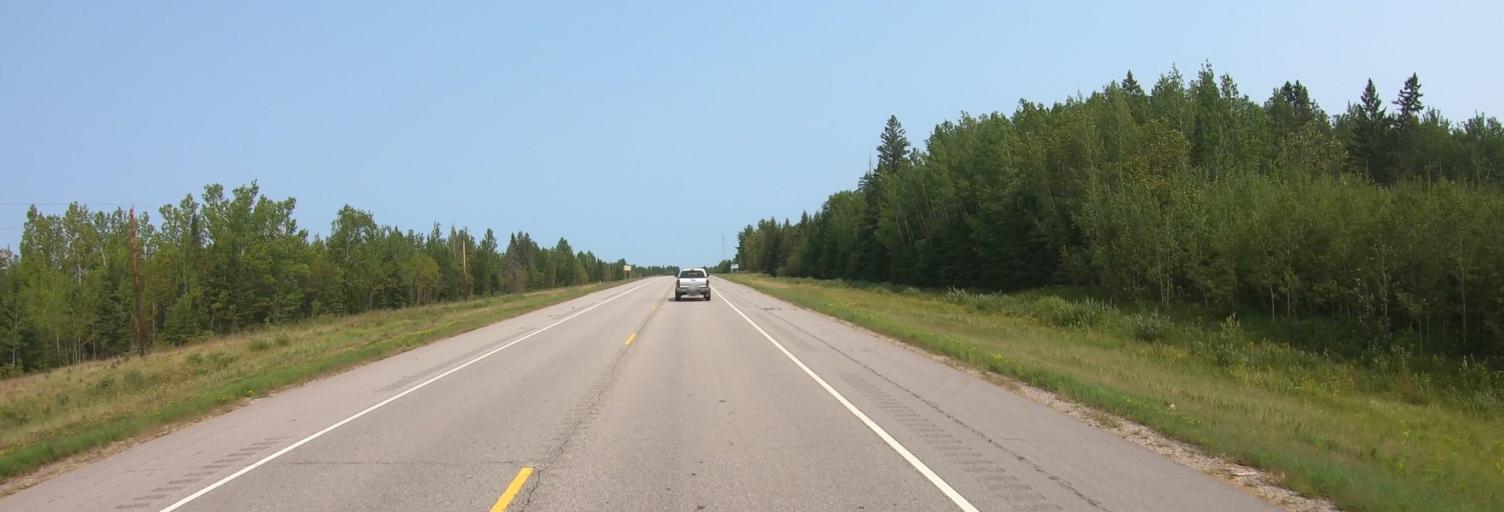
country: CA
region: Ontario
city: Fort Frances
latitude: 48.3326
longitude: -92.9630
